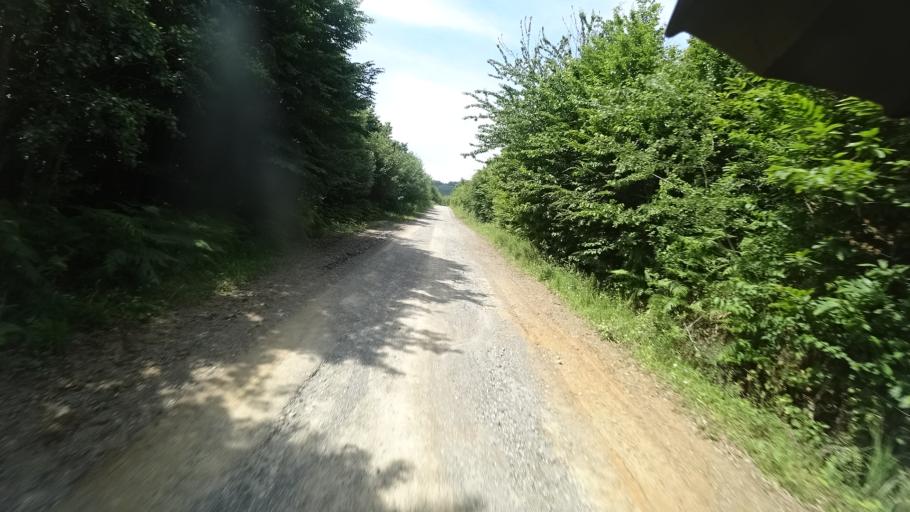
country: HR
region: Sisacko-Moslavacka
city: Gvozd
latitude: 45.3241
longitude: 15.8234
